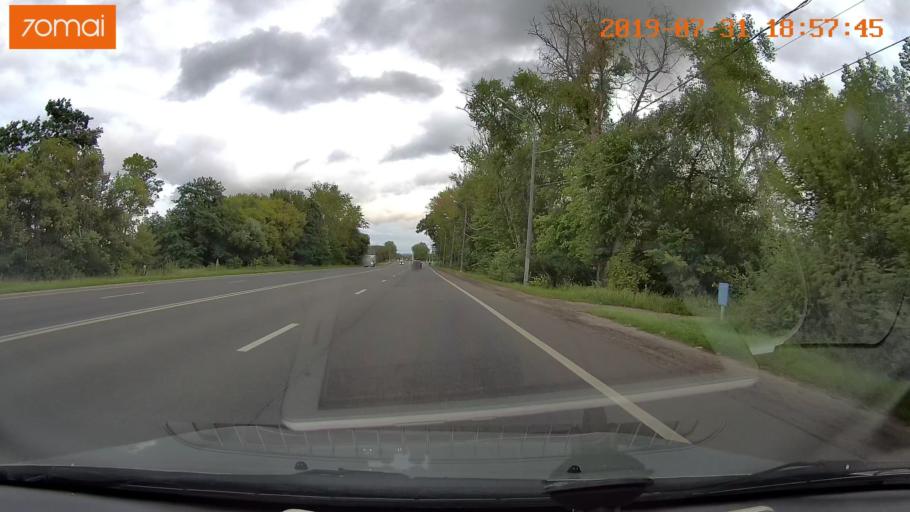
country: RU
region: Moskovskaya
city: Raduzhnyy
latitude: 55.1518
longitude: 38.6959
